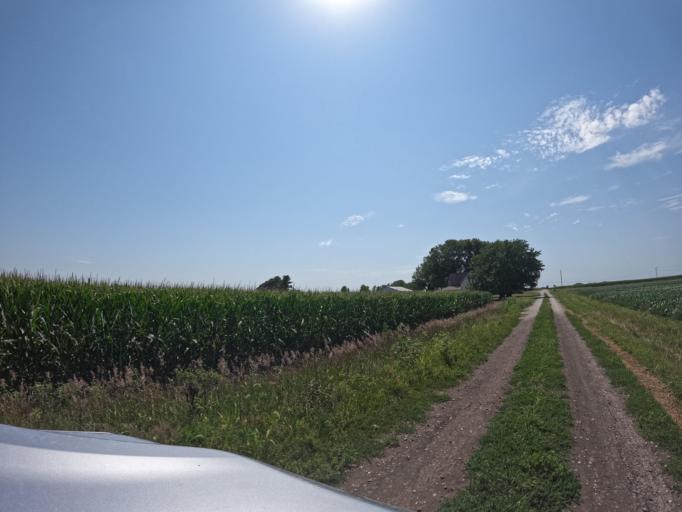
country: US
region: Iowa
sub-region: Henry County
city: Mount Pleasant
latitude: 40.9013
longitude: -91.6298
